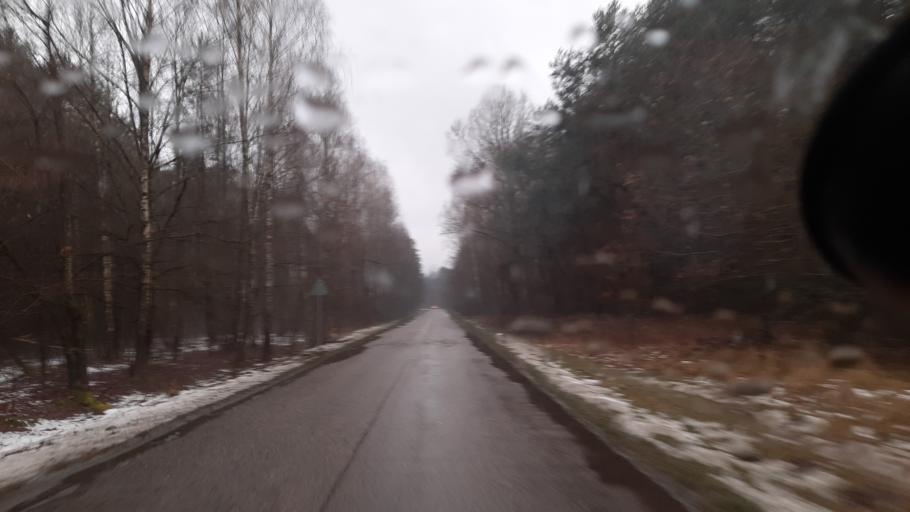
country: PL
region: Lublin Voivodeship
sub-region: Powiat lubartowski
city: Firlej
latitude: 51.5132
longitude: 22.4935
